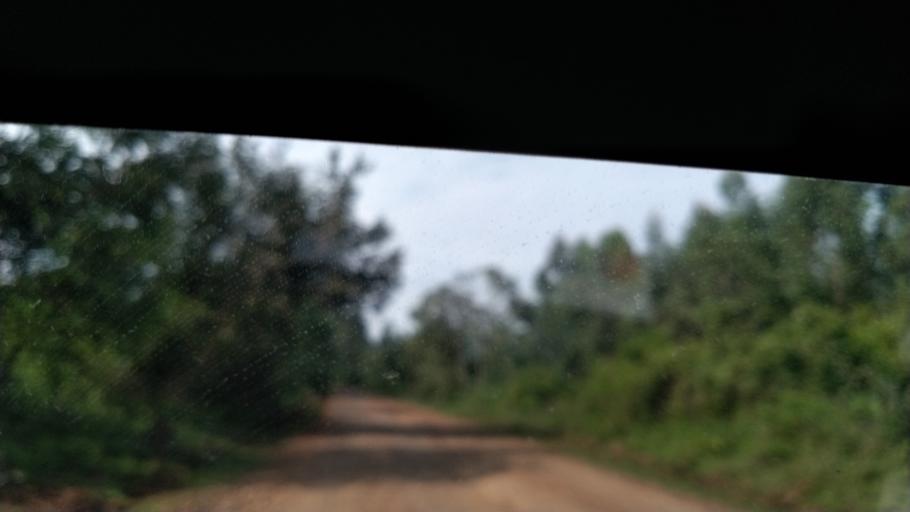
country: ET
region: Oromiya
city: Jima
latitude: 7.6672
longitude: 37.2448
